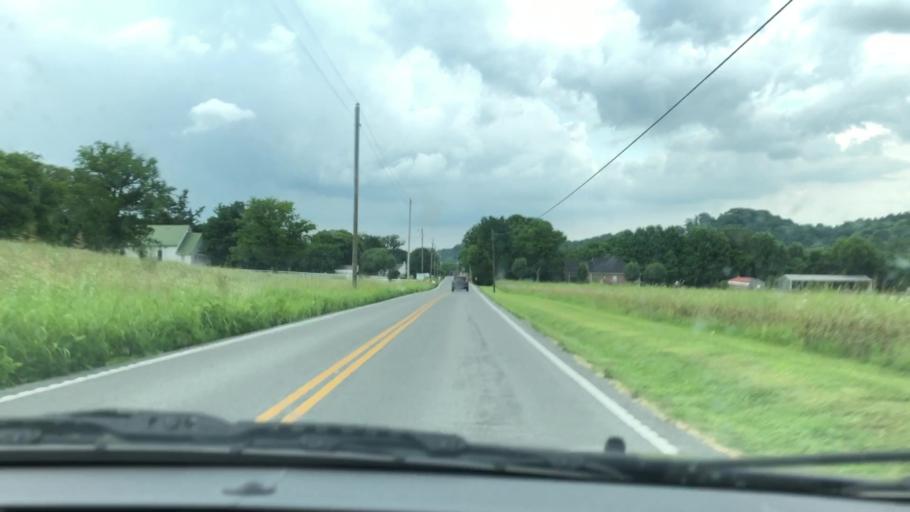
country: US
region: Tennessee
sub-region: Williamson County
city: Thompson's Station
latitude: 35.8095
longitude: -86.9879
